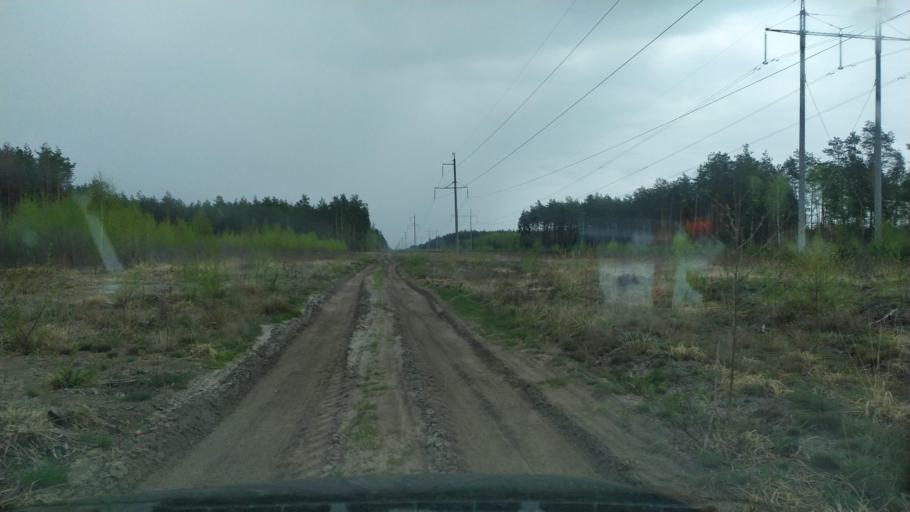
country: BY
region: Brest
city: Pruzhany
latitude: 52.3623
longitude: 24.5942
